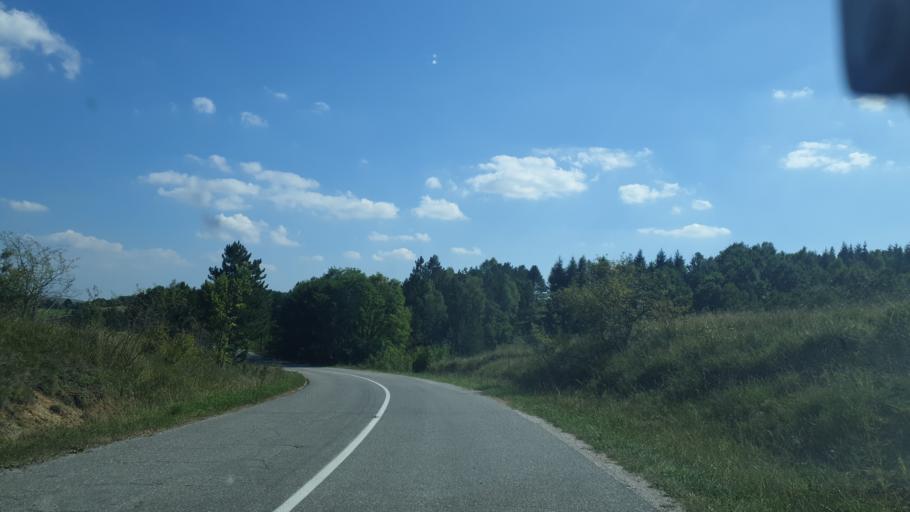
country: RS
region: Central Serbia
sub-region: Zlatiborski Okrug
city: Kosjeric
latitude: 44.0557
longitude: 20.0291
